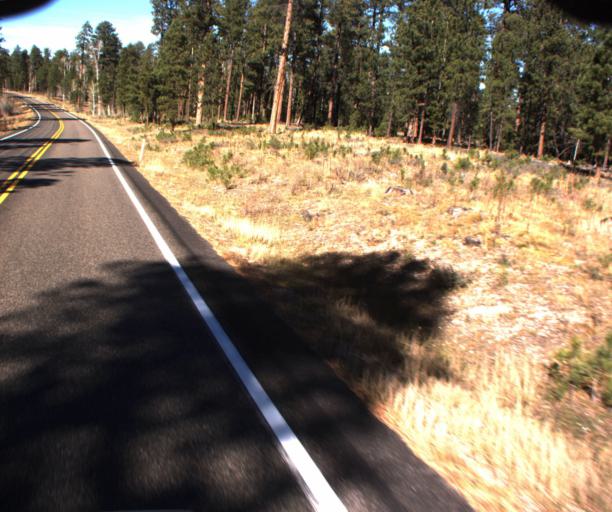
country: US
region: Arizona
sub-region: Coconino County
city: Fredonia
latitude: 36.6492
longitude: -112.1828
